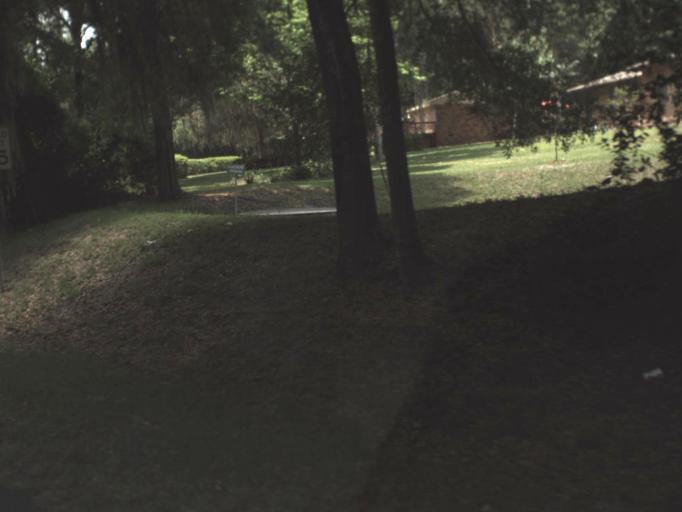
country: US
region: Florida
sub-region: Clay County
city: Keystone Heights
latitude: 29.7708
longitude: -82.0395
